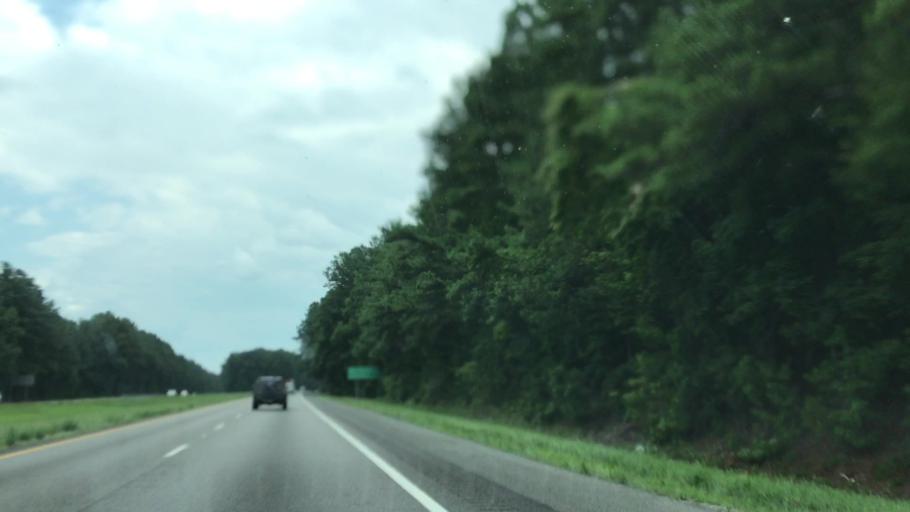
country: US
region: South Carolina
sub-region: Richland County
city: Blythewood
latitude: 34.2669
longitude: -80.9981
